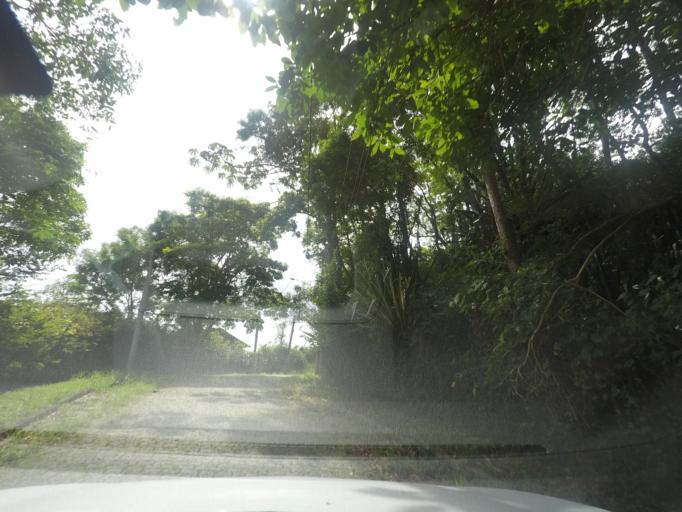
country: BR
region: Rio de Janeiro
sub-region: Teresopolis
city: Teresopolis
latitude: -22.3935
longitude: -42.9881
